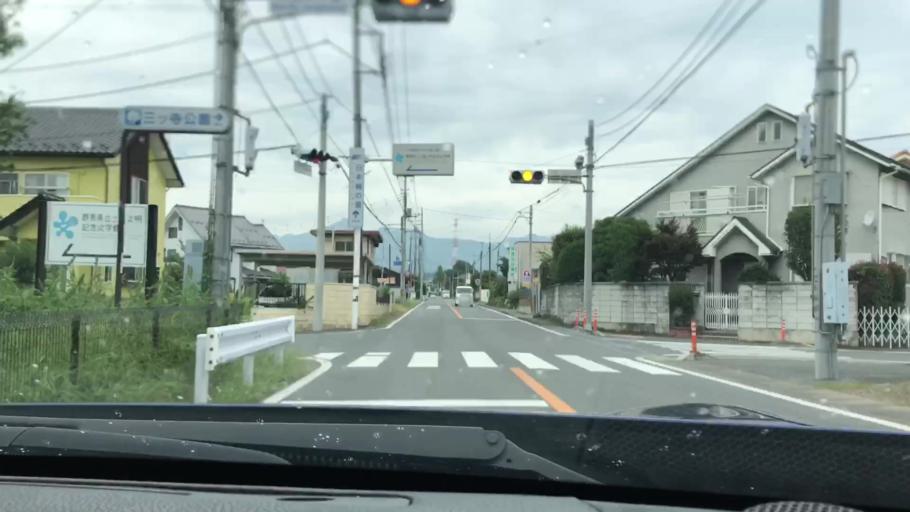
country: JP
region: Gunma
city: Kanekomachi
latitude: 36.3835
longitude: 138.9858
